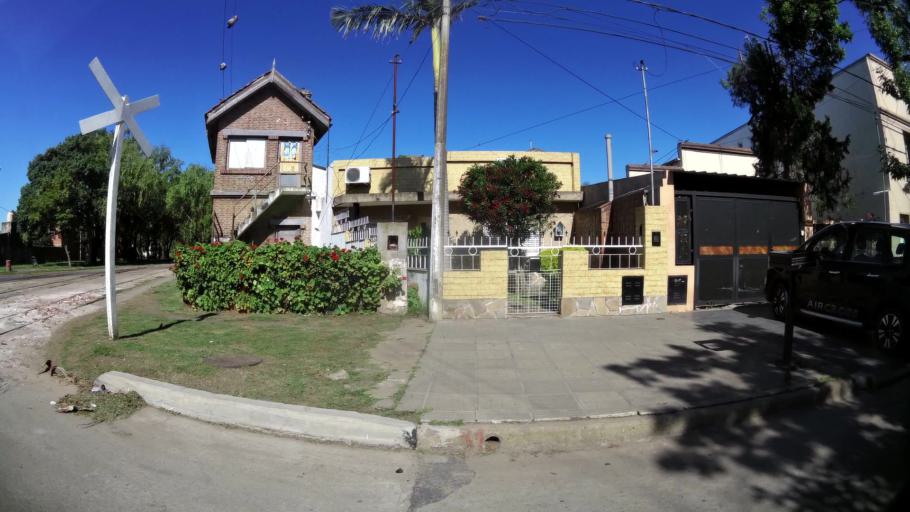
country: AR
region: Santa Fe
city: Santa Fe de la Vera Cruz
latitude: -31.6283
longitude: -60.6883
